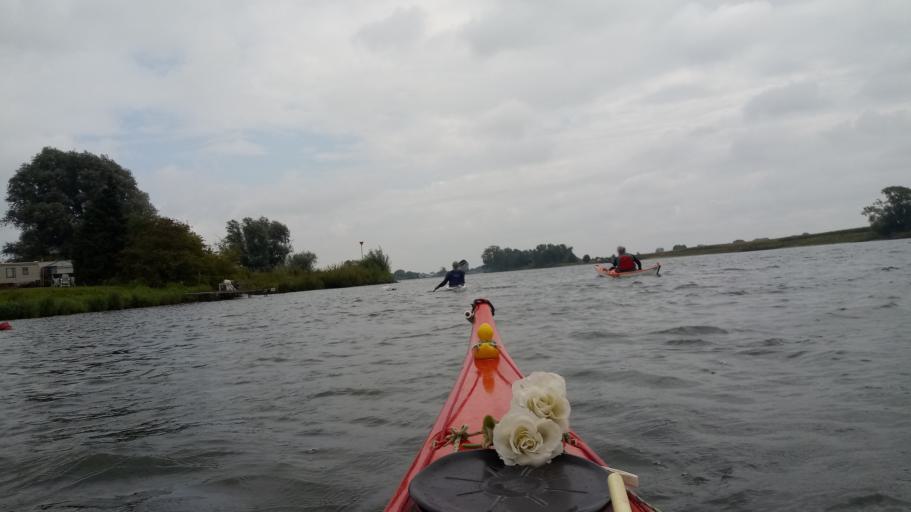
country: NL
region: Gelderland
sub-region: Gemeente Zaltbommel
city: Nederhemert-Noord
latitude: 51.7415
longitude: 5.2024
